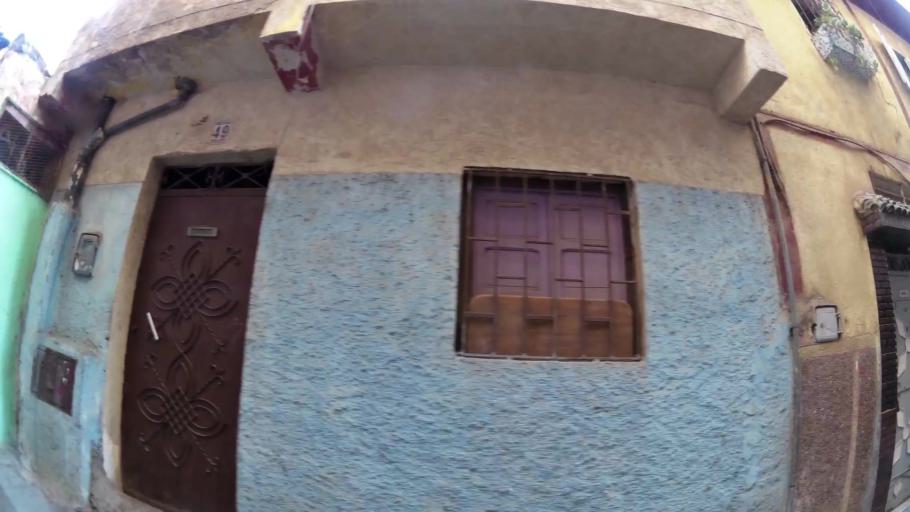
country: MA
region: Rabat-Sale-Zemmour-Zaer
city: Sale
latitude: 34.0591
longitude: -6.7860
